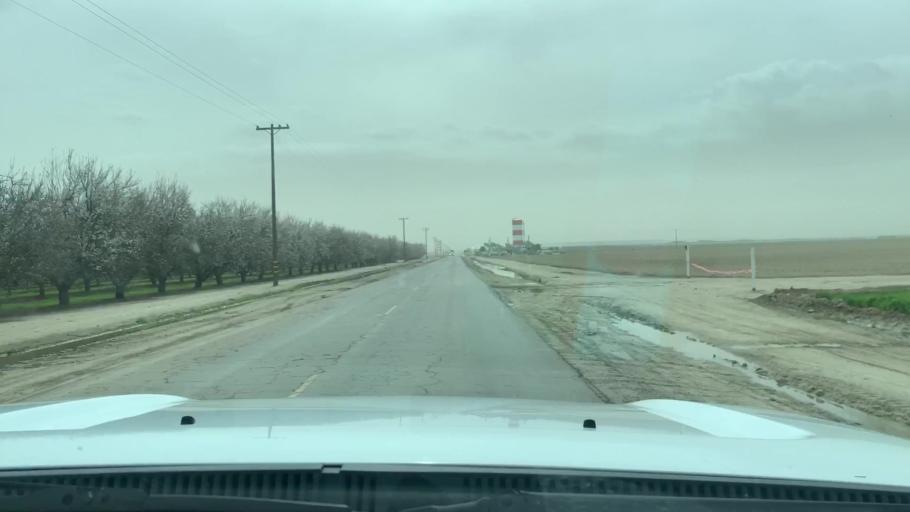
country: US
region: California
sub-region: Kern County
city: Wasco
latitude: 35.5618
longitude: -119.4029
